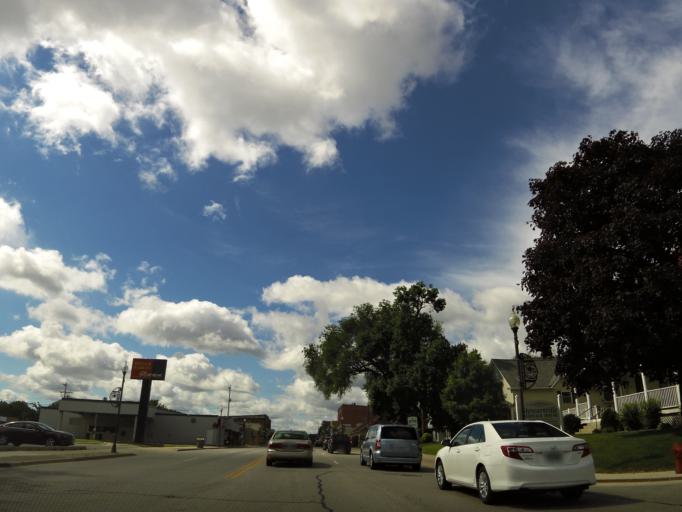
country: US
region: Minnesota
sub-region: Olmsted County
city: Stewartville
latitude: 43.8577
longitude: -92.4886
